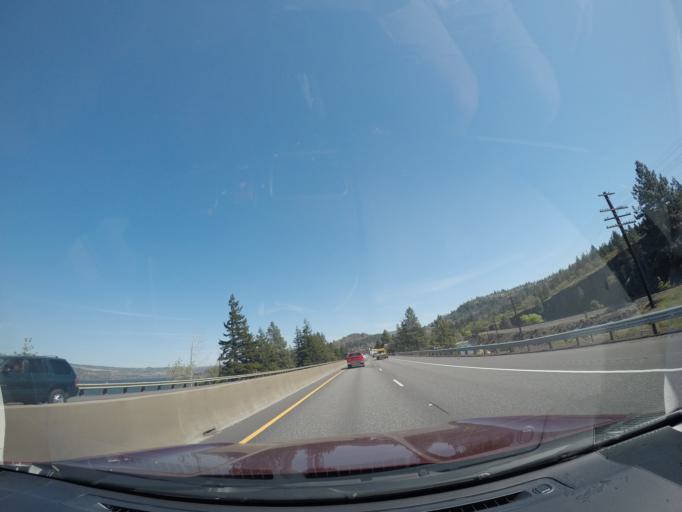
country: US
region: Washington
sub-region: Klickitat County
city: White Salmon
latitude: 45.6876
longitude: -121.4104
